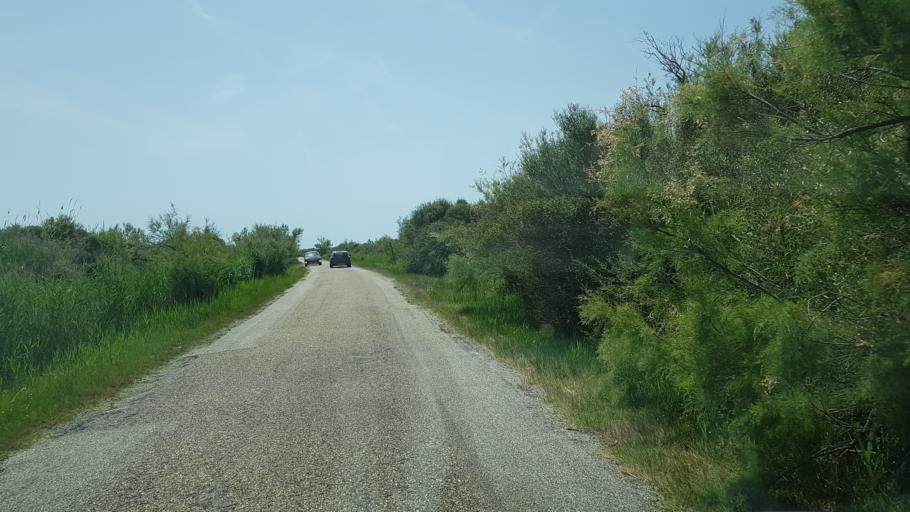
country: FR
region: Provence-Alpes-Cote d'Azur
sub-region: Departement des Bouches-du-Rhone
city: Port-Saint-Louis-du-Rhone
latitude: 43.4778
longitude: 4.6481
